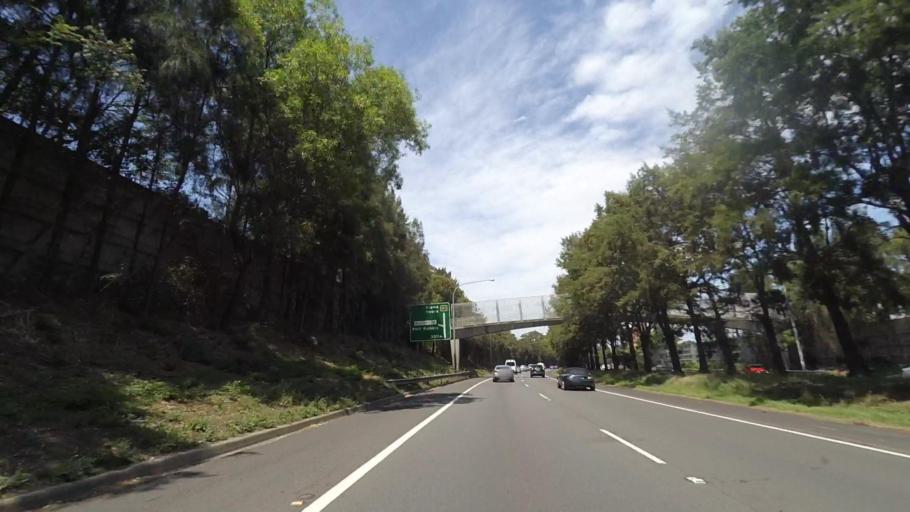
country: AU
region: New South Wales
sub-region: Wollongong
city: Mangerton
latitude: -34.4345
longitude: 150.8686
